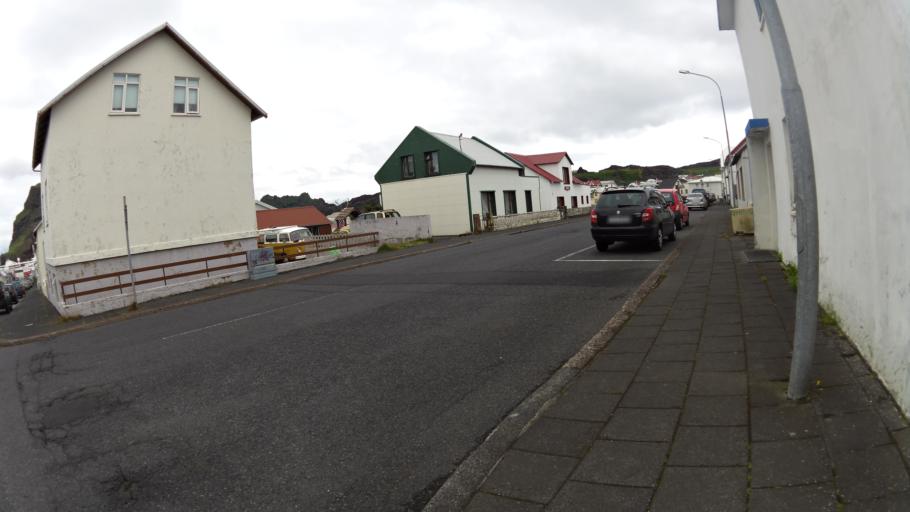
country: IS
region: South
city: Vestmannaeyjar
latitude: 63.4383
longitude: -20.2707
